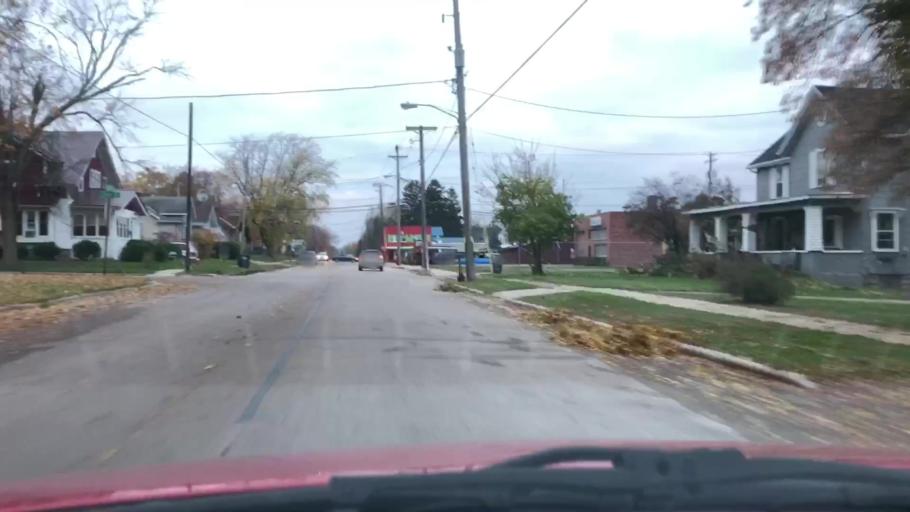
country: US
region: Wisconsin
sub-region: Outagamie County
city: Seymour
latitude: 44.5105
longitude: -88.3285
